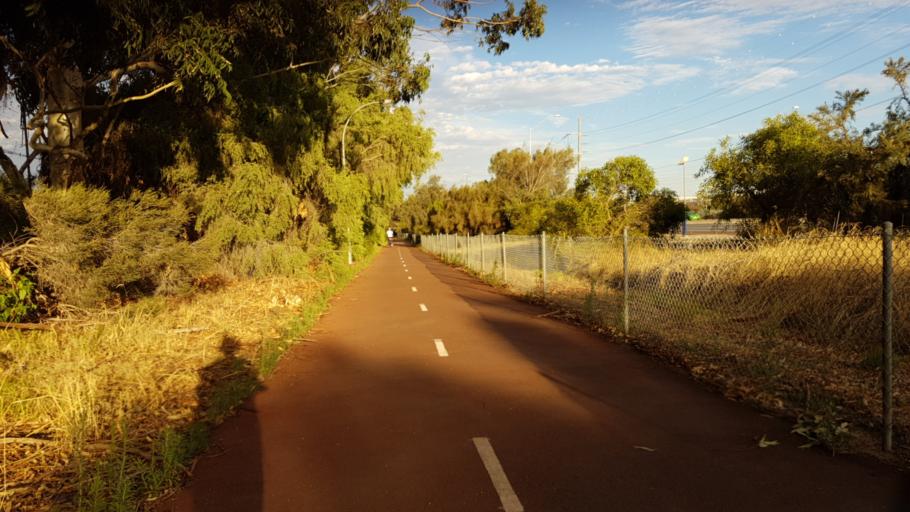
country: AU
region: Western Australia
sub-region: Canning
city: Canning Vale
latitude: -32.0544
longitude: 115.9189
